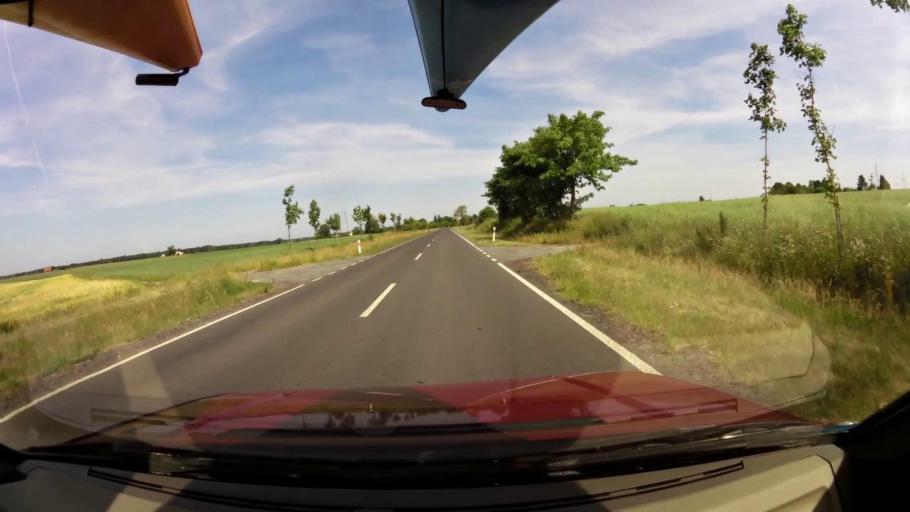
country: PL
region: West Pomeranian Voivodeship
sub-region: Powiat koszalinski
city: Sianow
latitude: 54.3042
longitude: 16.3070
